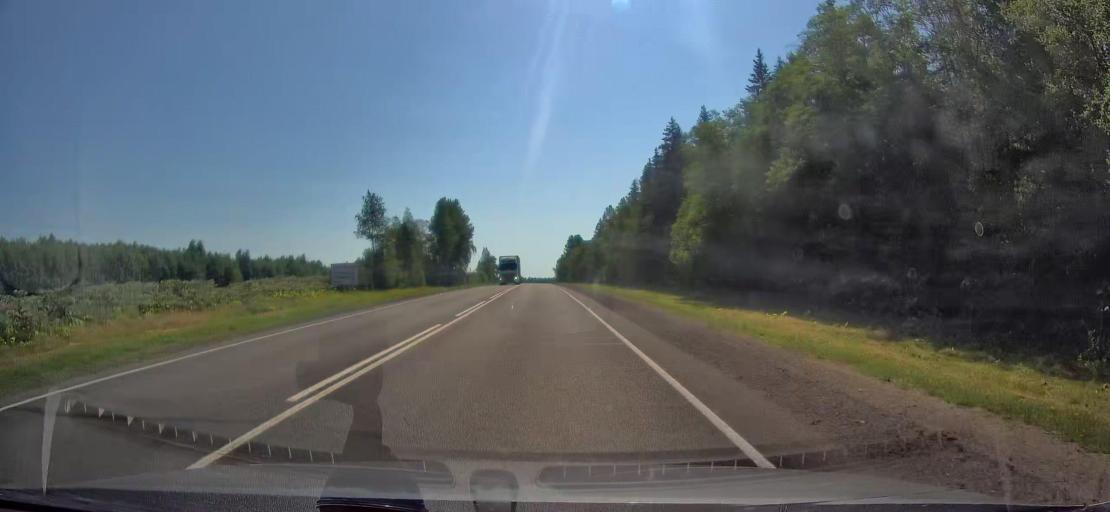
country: RU
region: Vologda
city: Sazonovo
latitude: 59.0877
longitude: 35.2728
